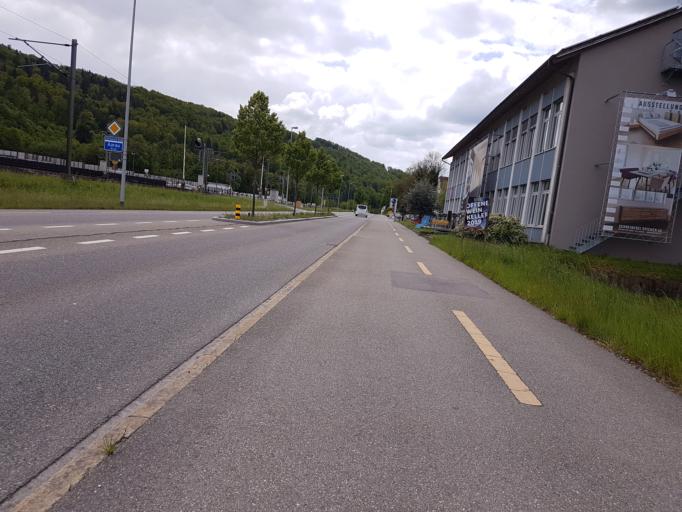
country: CH
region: Aargau
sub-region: Bezirk Brugg
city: Brugg
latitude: 47.4723
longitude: 8.1949
